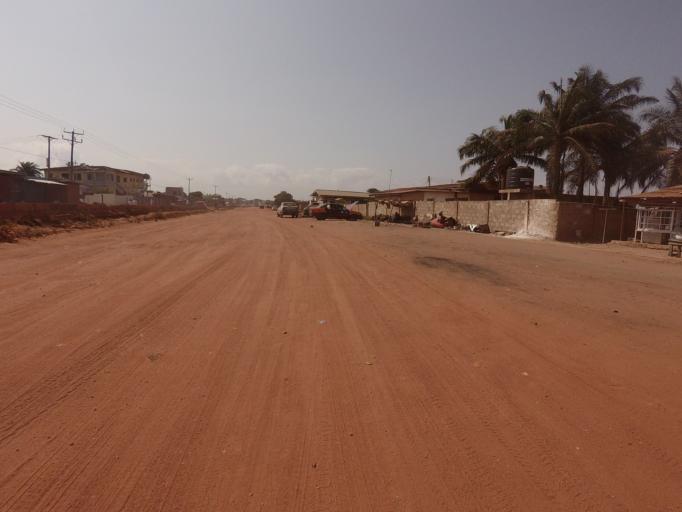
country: GH
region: Greater Accra
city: Teshi Old Town
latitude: 5.5834
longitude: -0.1135
